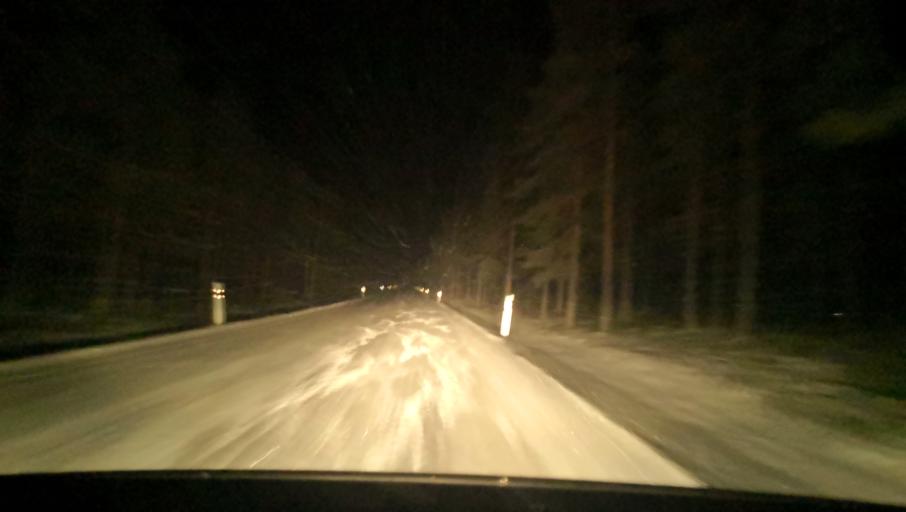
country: SE
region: Uppsala
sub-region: Heby Kommun
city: Tarnsjo
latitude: 60.1251
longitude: 16.8871
